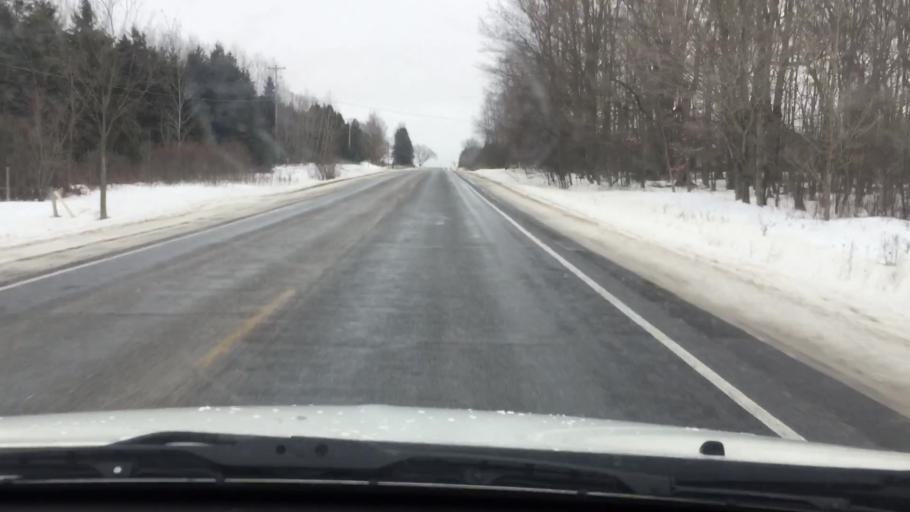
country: US
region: Michigan
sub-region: Osceola County
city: Reed City
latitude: 44.0492
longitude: -85.4439
